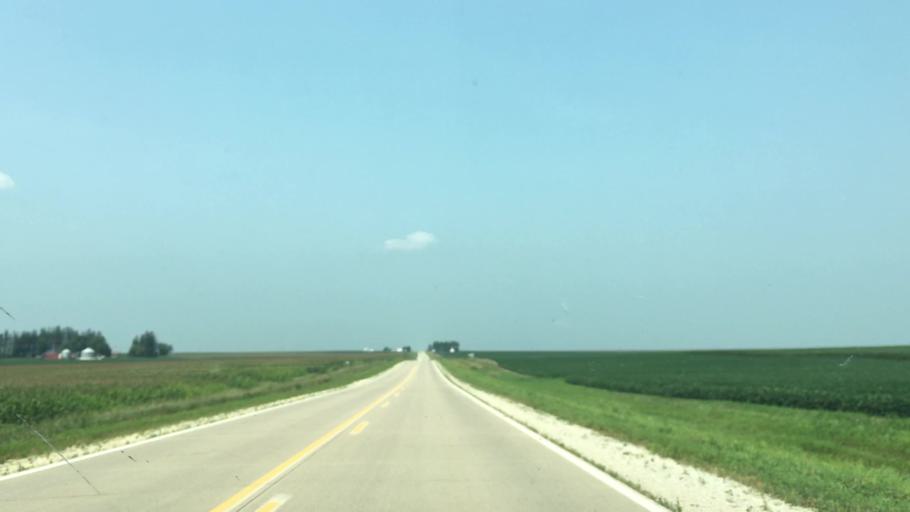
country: US
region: Iowa
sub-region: Fayette County
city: Oelwein
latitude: 42.6953
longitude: -91.8050
